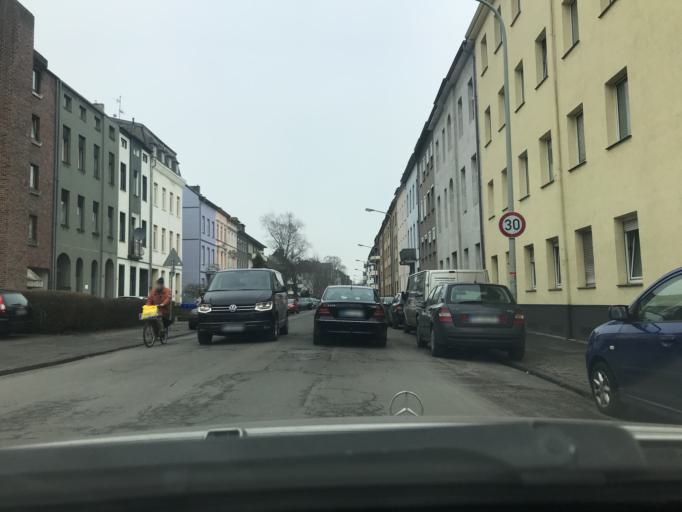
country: DE
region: North Rhine-Westphalia
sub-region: Regierungsbezirk Dusseldorf
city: Krefeld
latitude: 51.3196
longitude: 6.5595
